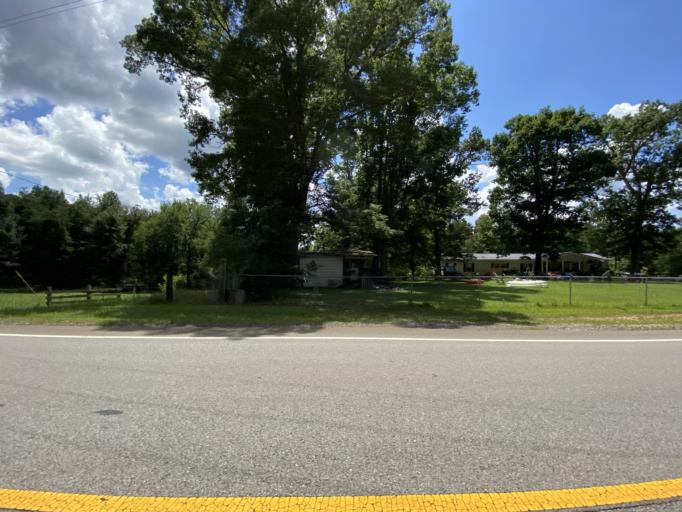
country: US
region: Alabama
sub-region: Lauderdale County
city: Underwood-Petersville
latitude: 34.9571
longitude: -87.8766
